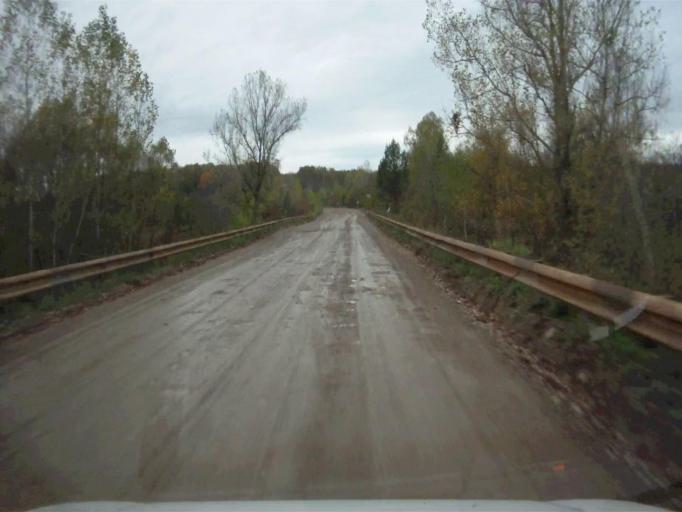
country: RU
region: Chelyabinsk
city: Nyazepetrovsk
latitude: 56.1325
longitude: 59.3180
